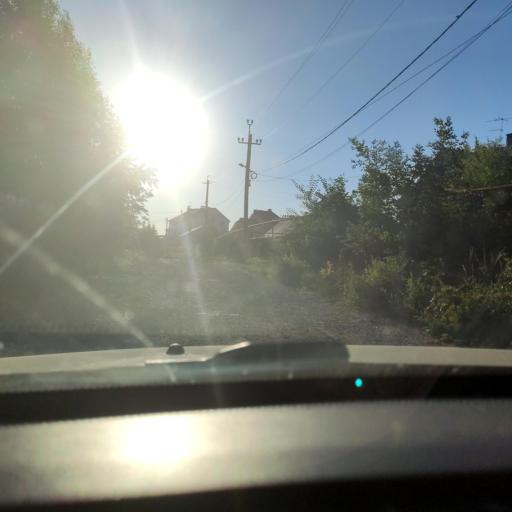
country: RU
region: Samara
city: Kinel'
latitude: 53.2726
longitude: 50.5920
